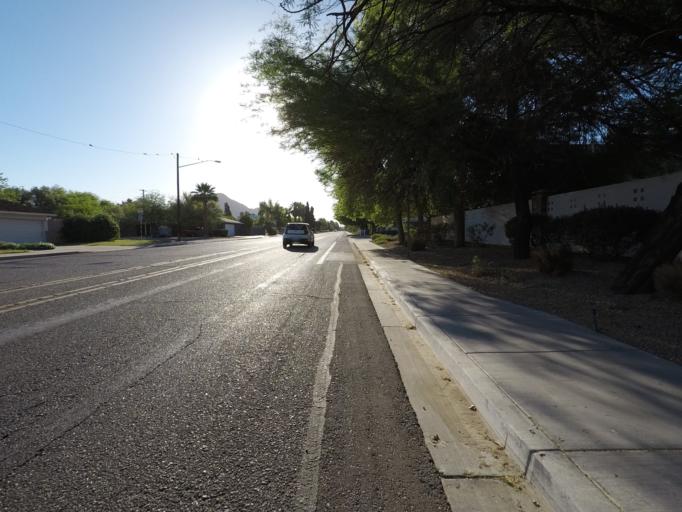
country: US
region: Arizona
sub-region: Maricopa County
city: Paradise Valley
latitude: 33.5025
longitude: -112.0030
